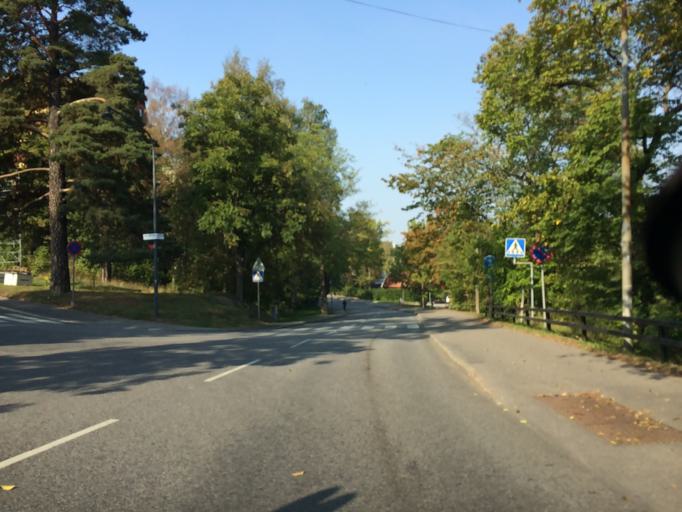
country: SE
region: Stockholm
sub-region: Solna Kommun
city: Solna
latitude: 59.3392
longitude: 18.0159
